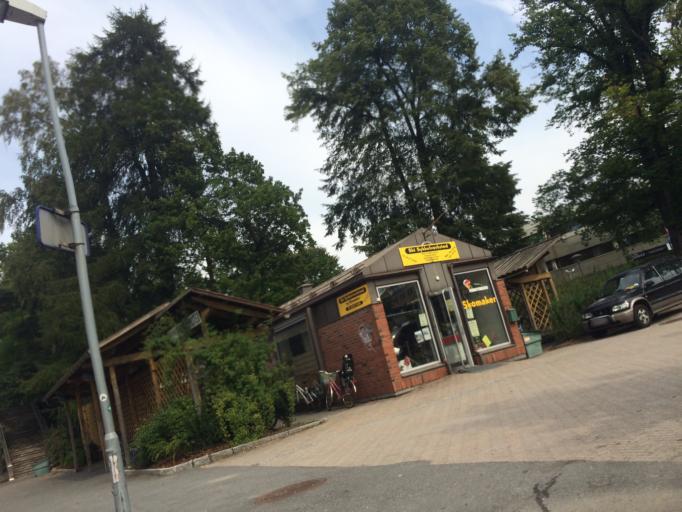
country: NO
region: Akershus
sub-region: Ski
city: Ski
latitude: 59.7195
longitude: 10.8350
